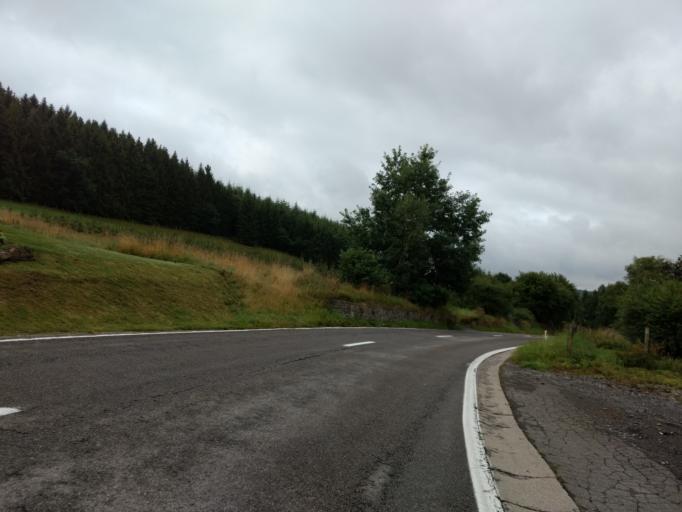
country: BE
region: Wallonia
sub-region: Province du Luxembourg
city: Houffalize
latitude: 50.1440
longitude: 5.7190
